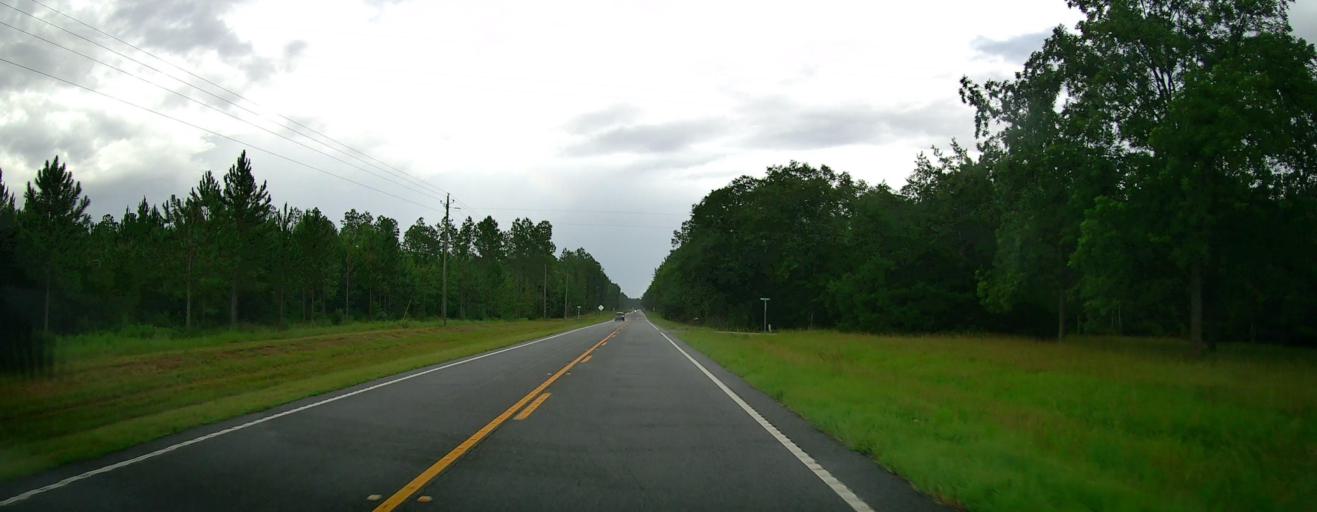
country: US
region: Georgia
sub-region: Ware County
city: Deenwood
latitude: 31.2791
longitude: -82.5384
